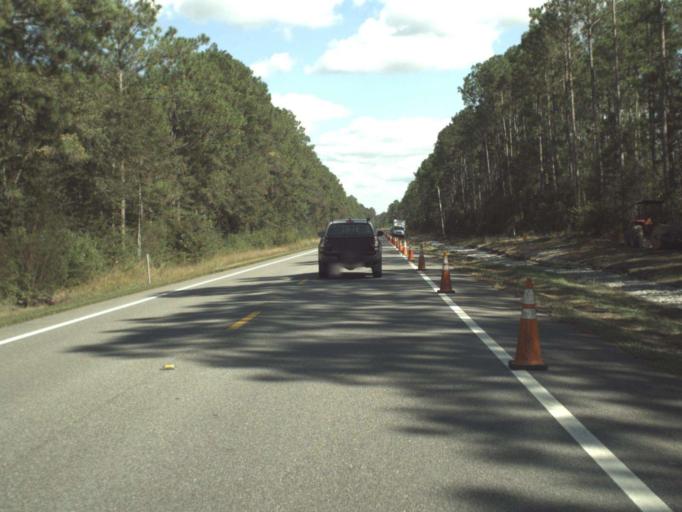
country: US
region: Florida
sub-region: Walton County
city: Freeport
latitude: 30.4736
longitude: -85.9824
